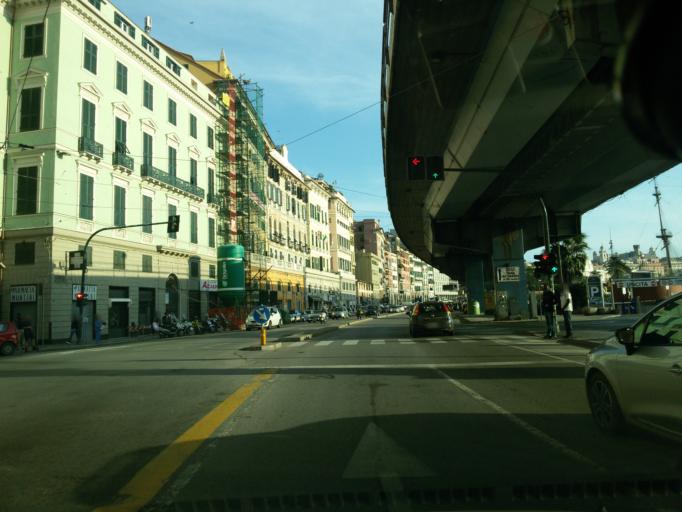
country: IT
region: Liguria
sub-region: Provincia di Genova
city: San Teodoro
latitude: 44.4130
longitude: 8.9267
